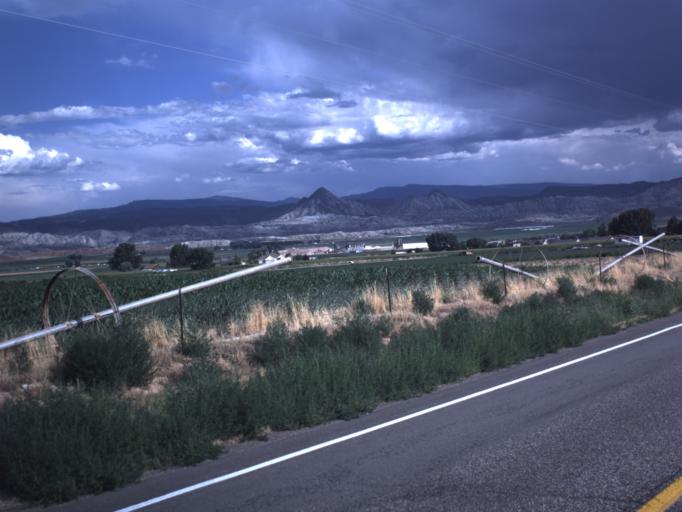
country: US
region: Utah
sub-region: Sevier County
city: Aurora
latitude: 38.9330
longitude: -111.9343
